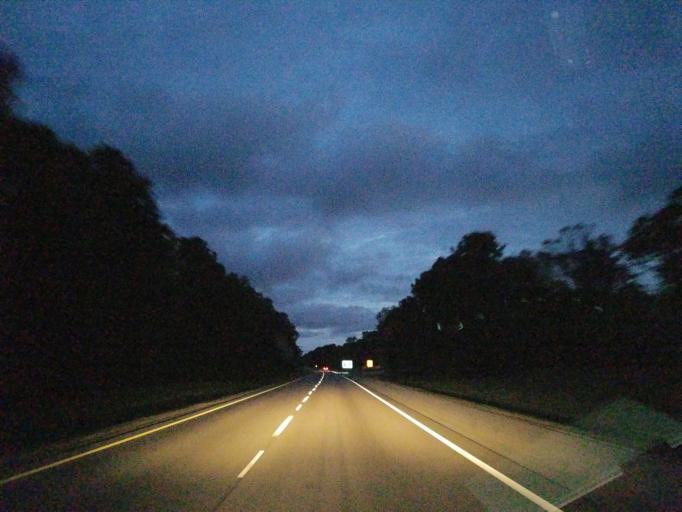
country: US
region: Mississippi
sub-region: Jones County
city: Sharon
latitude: 31.8550
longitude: -89.0485
